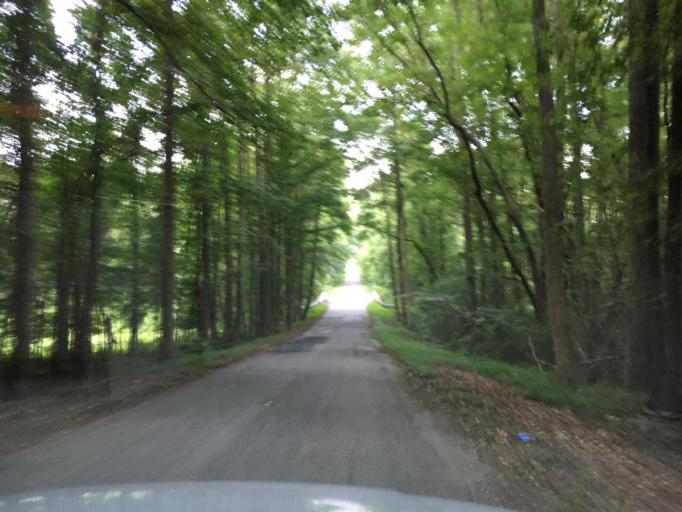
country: US
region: South Carolina
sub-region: Laurens County
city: Watts Mills
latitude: 34.5463
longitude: -81.9429
